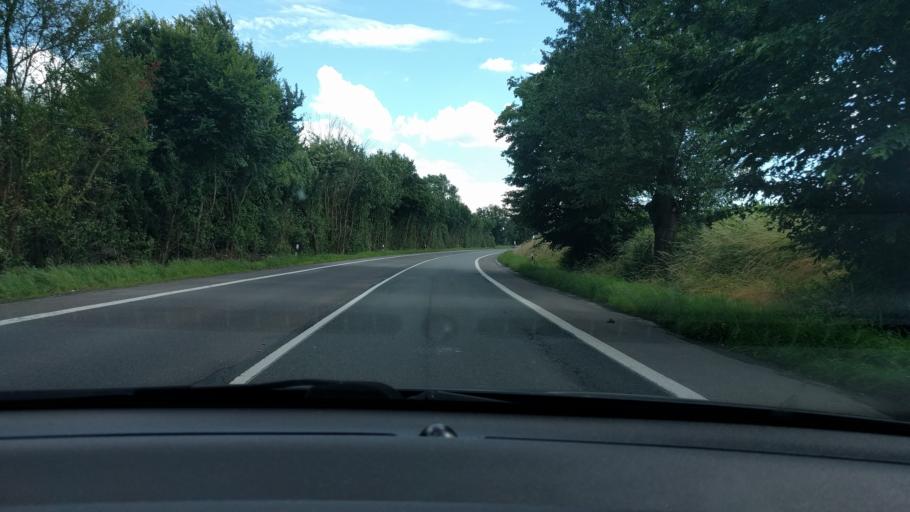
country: DE
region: North Rhine-Westphalia
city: Olfen
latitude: 51.6847
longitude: 7.3277
